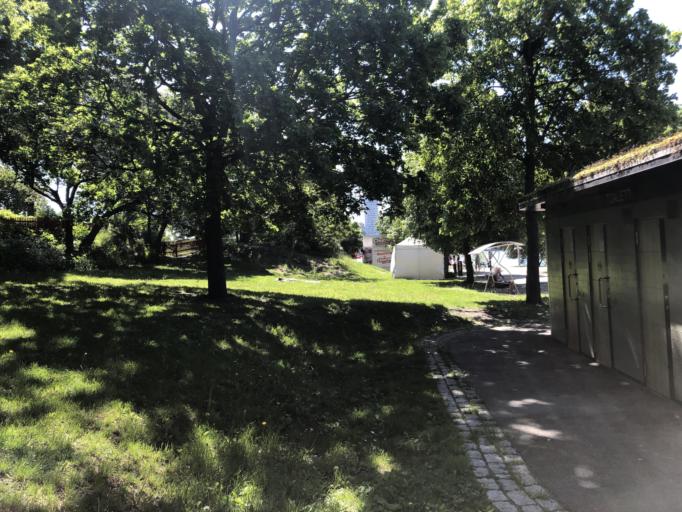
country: SE
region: Stockholm
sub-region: Stockholms Kommun
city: Arsta
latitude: 59.3127
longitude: 18.0382
